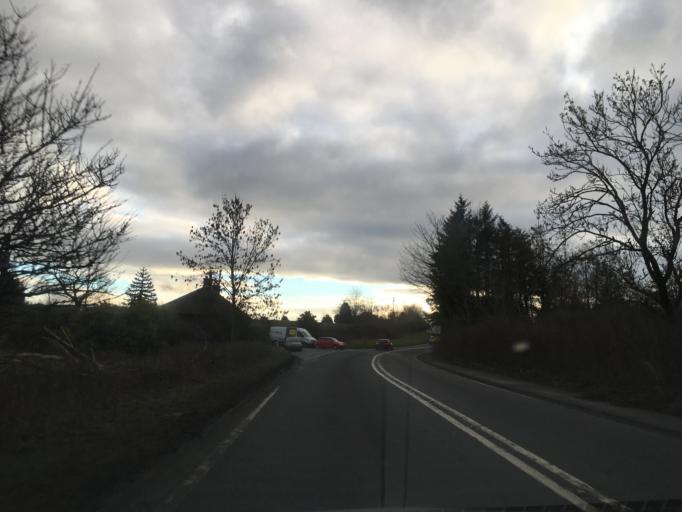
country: GB
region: Scotland
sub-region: Midlothian
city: Penicuik
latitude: 55.8666
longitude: -3.2127
